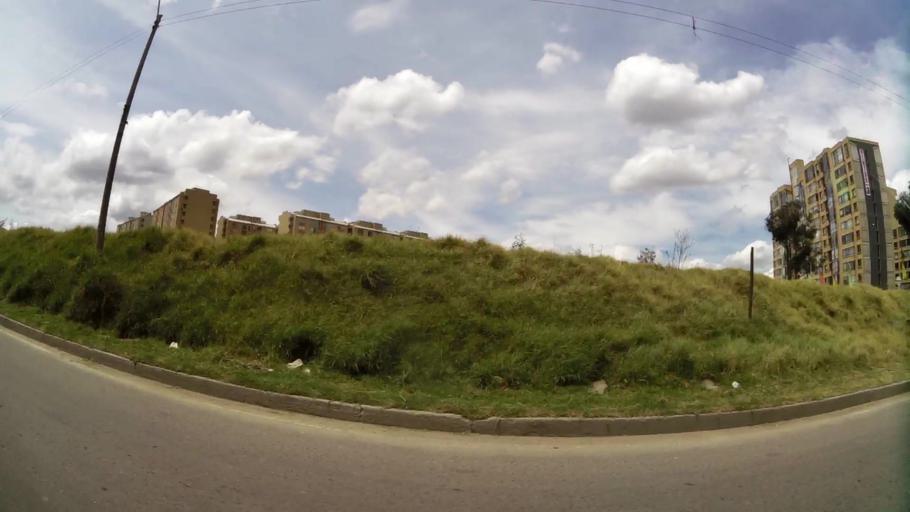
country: CO
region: Bogota D.C.
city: Bogota
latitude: 4.6480
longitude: -74.1344
